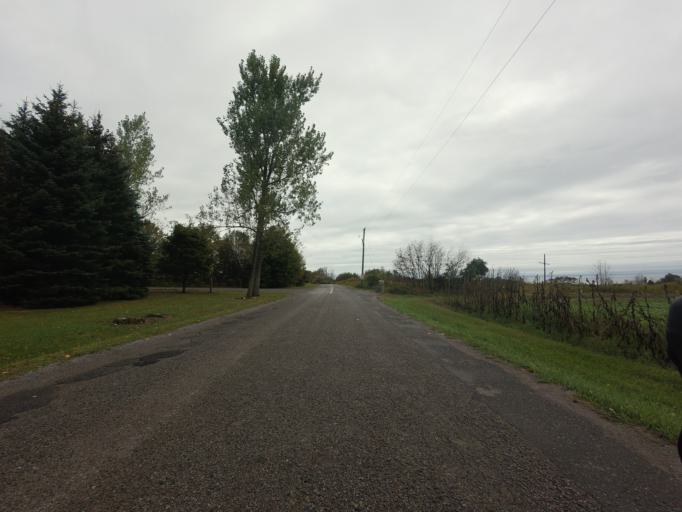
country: CA
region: Ontario
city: Oshawa
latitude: 43.9038
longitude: -78.5098
